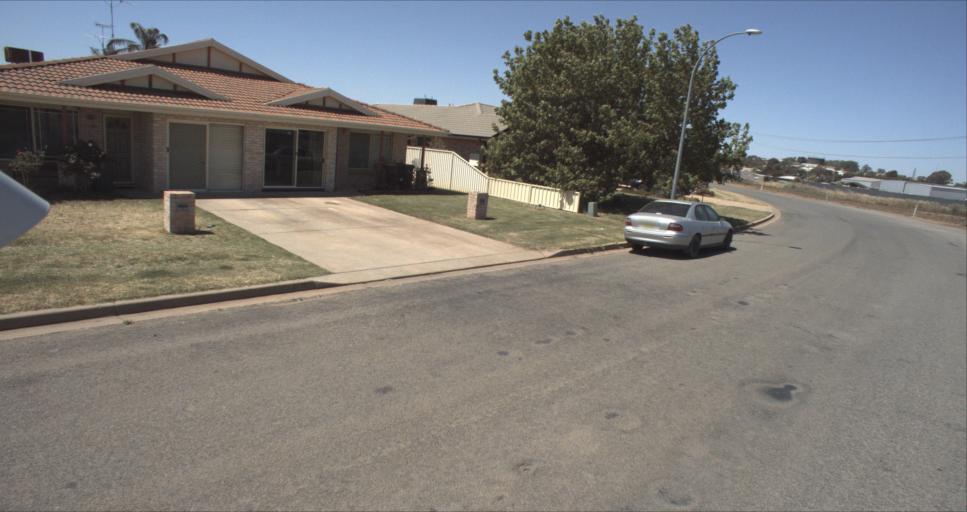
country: AU
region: New South Wales
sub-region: Leeton
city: Leeton
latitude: -34.5454
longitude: 146.3971
